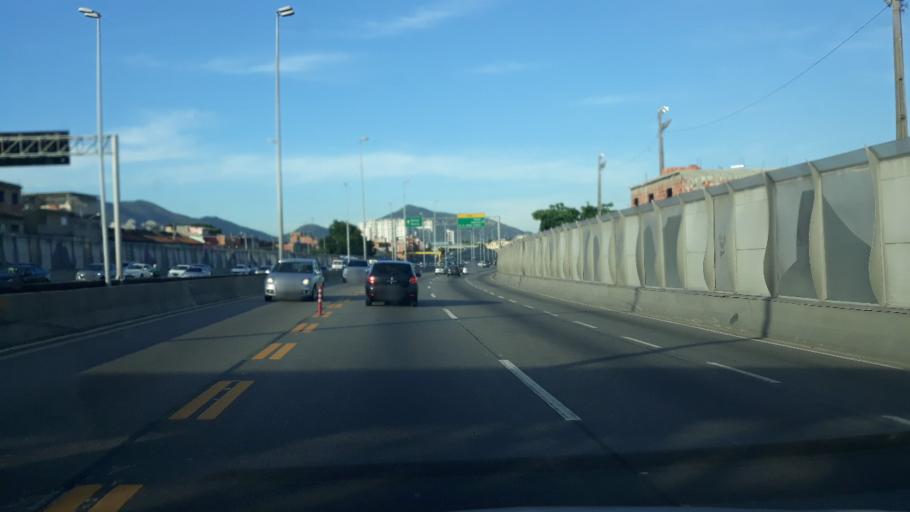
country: BR
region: Rio de Janeiro
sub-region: Rio De Janeiro
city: Rio de Janeiro
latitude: -22.8805
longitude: -43.2801
